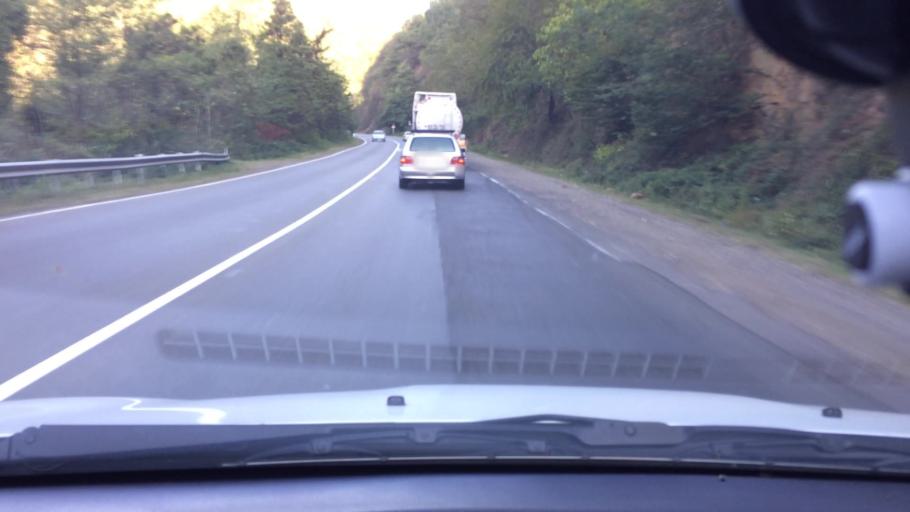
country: GE
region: Imereti
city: Kharagauli
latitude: 42.1055
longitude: 43.2058
